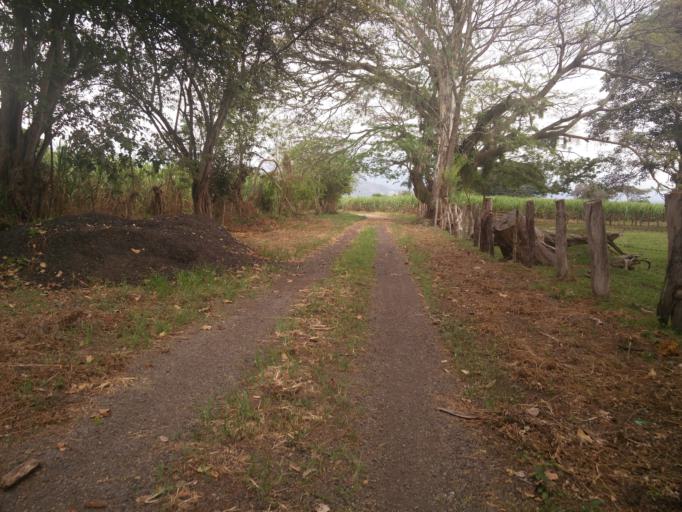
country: CO
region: Valle del Cauca
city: Buga
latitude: 3.8902
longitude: -76.3244
